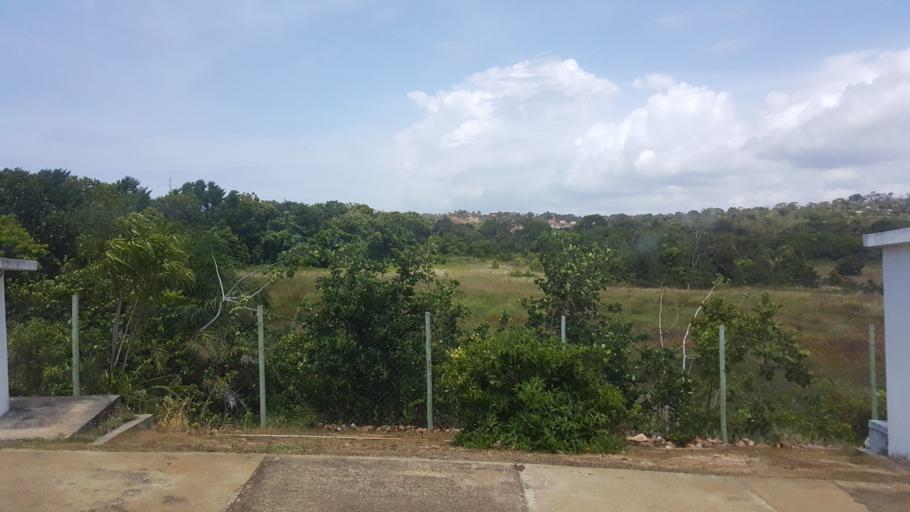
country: BR
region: Bahia
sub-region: Mata De Sao Joao
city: Mata de Sao Joao
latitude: -12.4820
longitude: -37.9618
